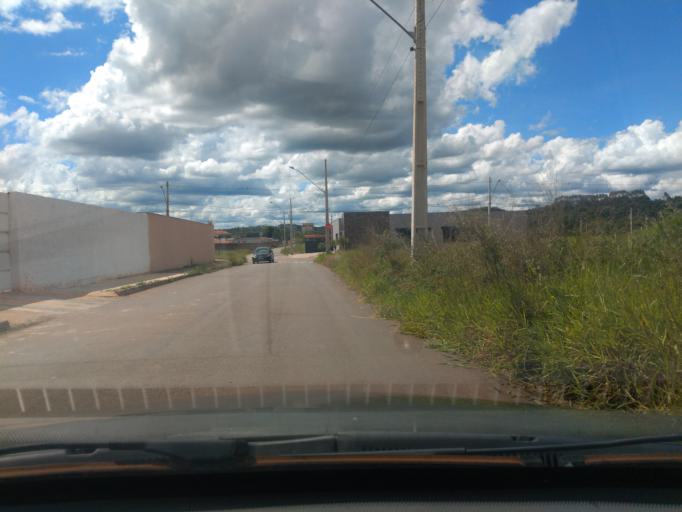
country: BR
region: Minas Gerais
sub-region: Tres Coracoes
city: Tres Coracoes
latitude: -21.6766
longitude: -45.2642
